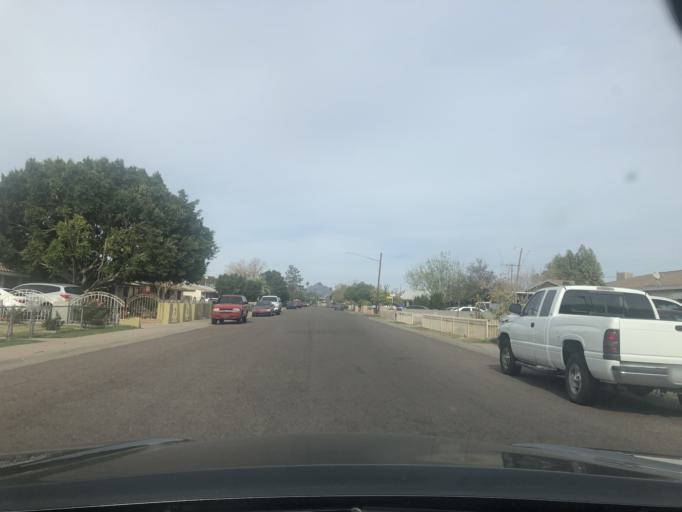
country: US
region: Arizona
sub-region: Maricopa County
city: Phoenix
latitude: 33.4549
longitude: -112.0211
